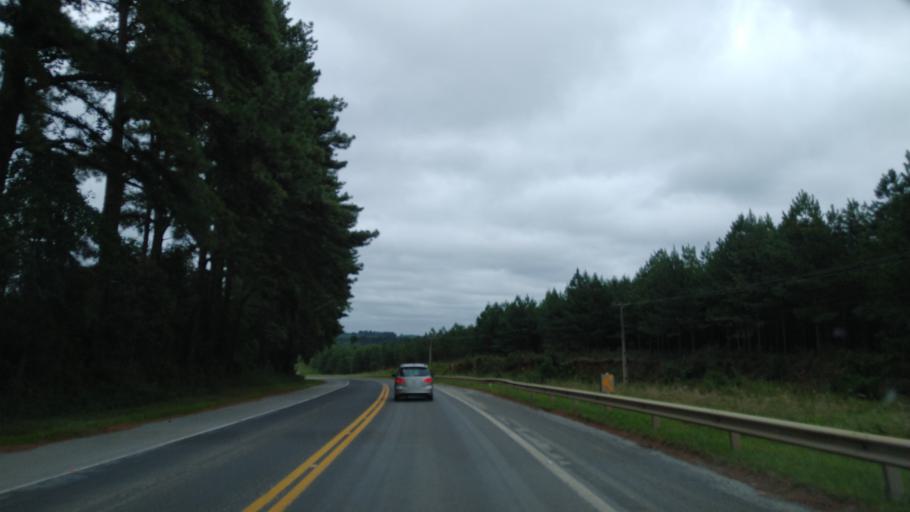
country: BR
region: Santa Catarina
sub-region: Tres Barras
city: Tres Barras
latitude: -26.1612
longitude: -50.1322
